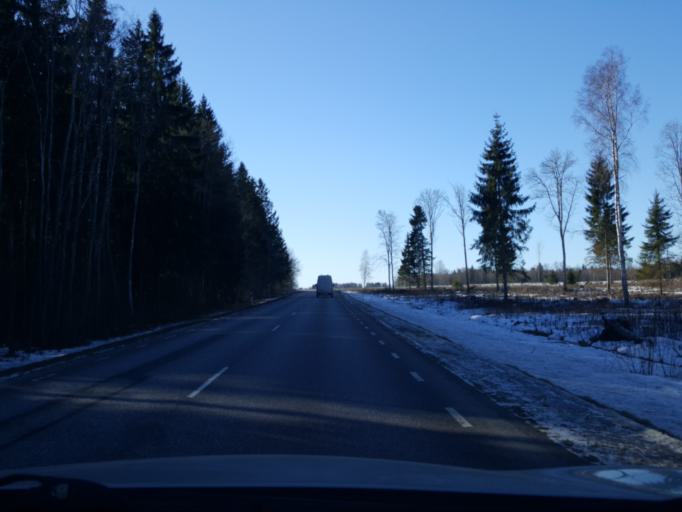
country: EE
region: Viljandimaa
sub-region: Viiratsi vald
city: Viiratsi
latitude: 58.4159
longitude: 25.6733
